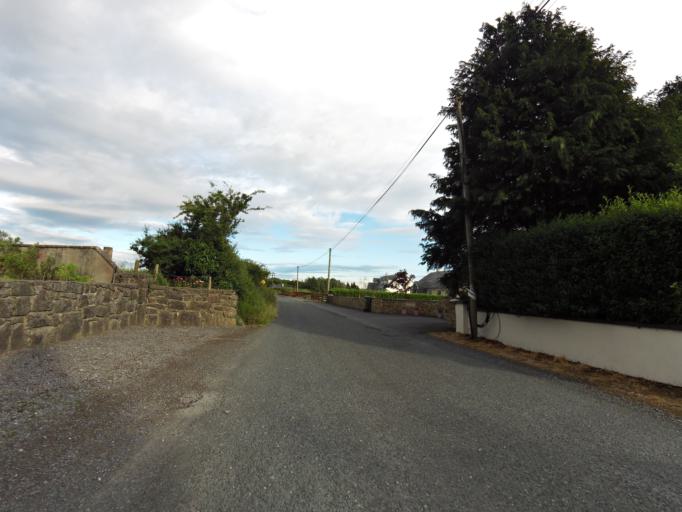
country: IE
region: Connaught
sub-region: County Galway
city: Athenry
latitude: 53.2962
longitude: -8.7337
